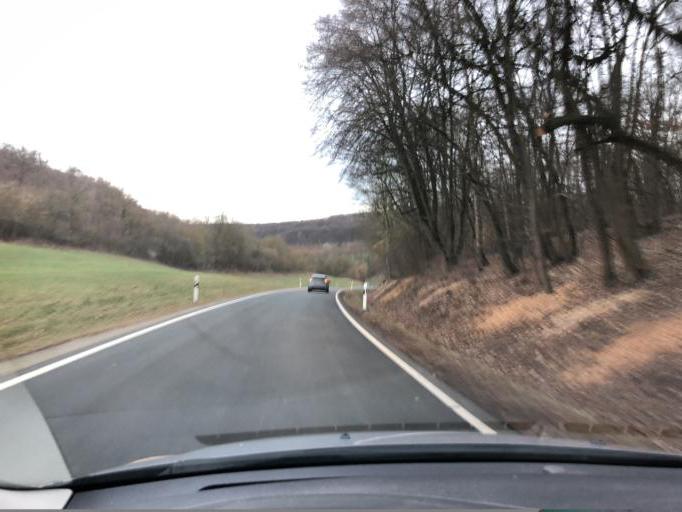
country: DE
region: Saxony-Anhalt
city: Laucha
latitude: 51.2078
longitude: 11.7043
